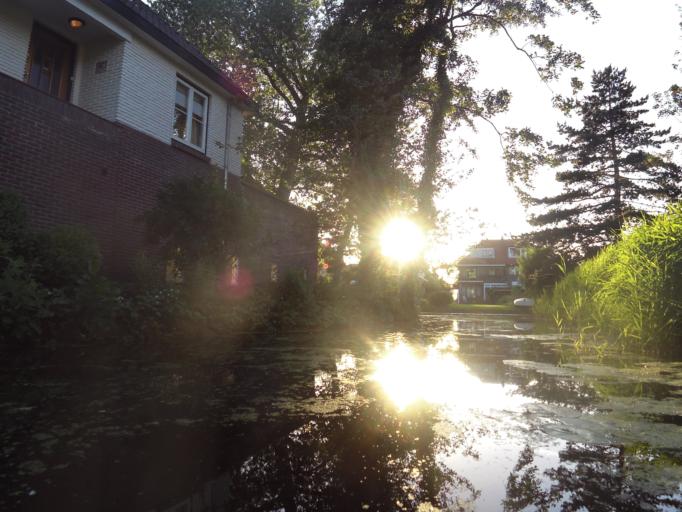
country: NL
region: South Holland
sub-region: Gemeente Wassenaar
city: Wassenaar
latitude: 52.1396
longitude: 4.3993
